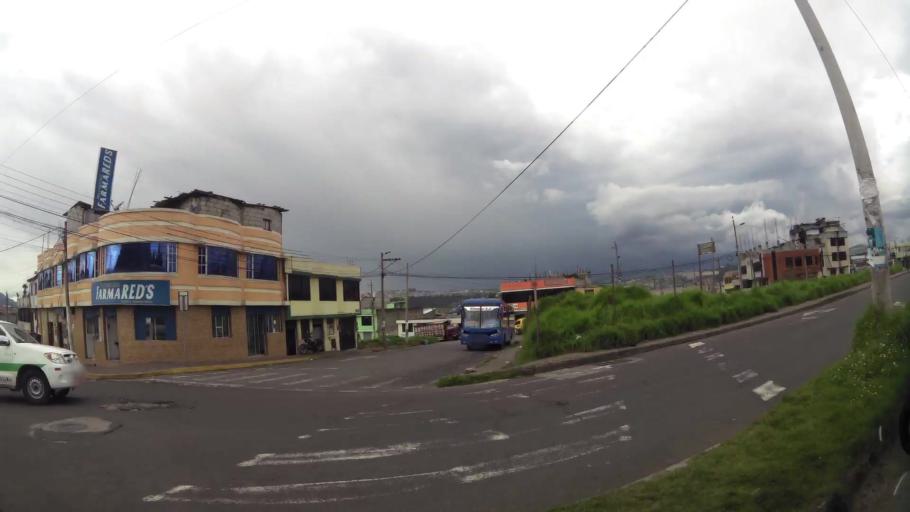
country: EC
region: Pichincha
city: Quito
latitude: -0.3237
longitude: -78.5544
